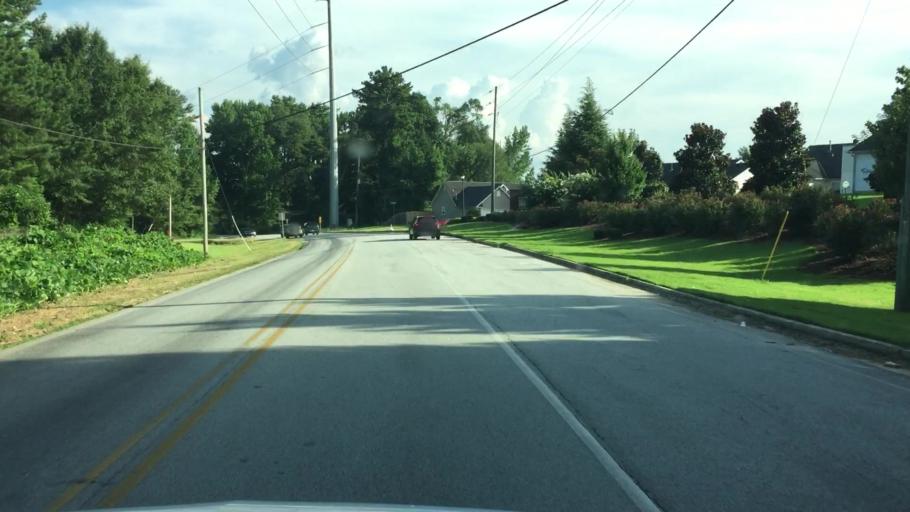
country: US
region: Georgia
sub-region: DeKalb County
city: Pine Mountain
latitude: 33.6372
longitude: -84.1296
